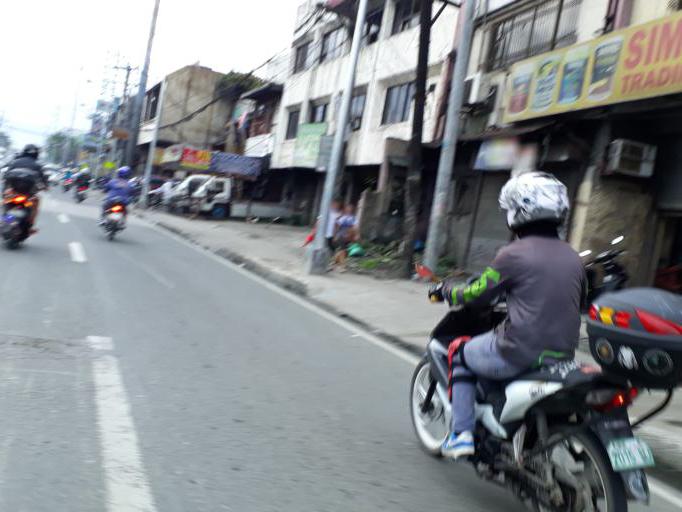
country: PH
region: Calabarzon
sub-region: Province of Rizal
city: Valenzuela
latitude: 14.6810
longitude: 120.9790
